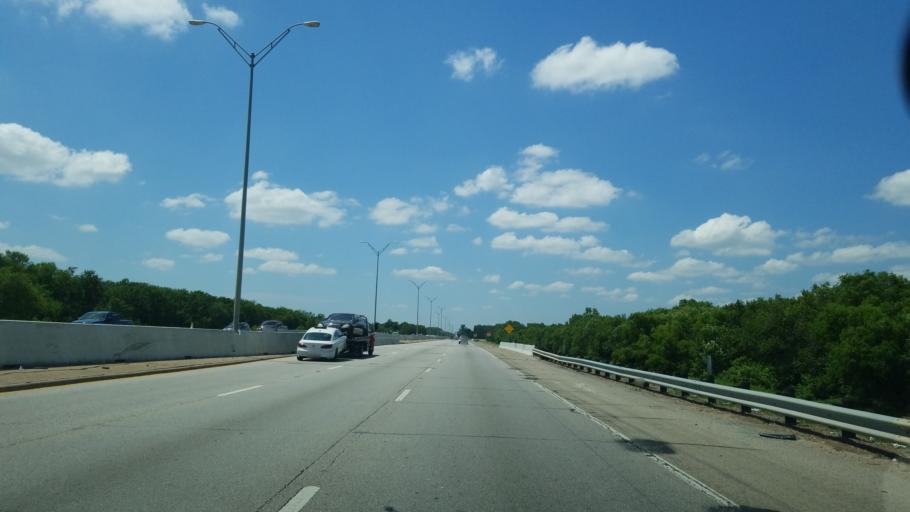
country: US
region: Texas
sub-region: Dallas County
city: Hutchins
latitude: 32.7375
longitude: -96.7169
